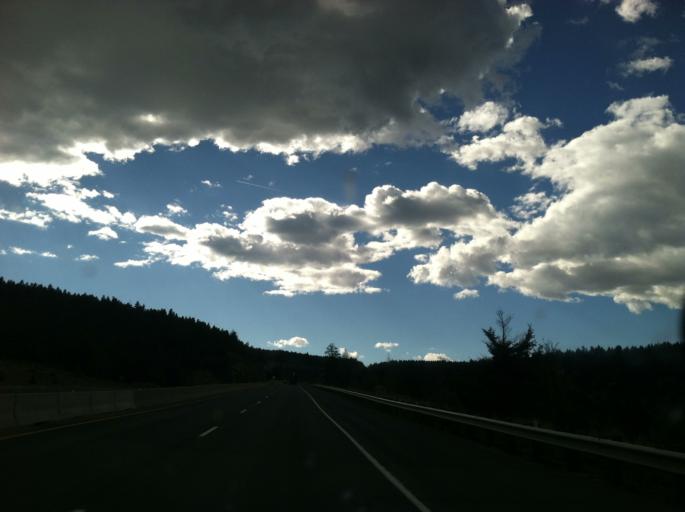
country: US
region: Montana
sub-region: Jefferson County
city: Whitehall
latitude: 45.9102
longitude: -112.3109
